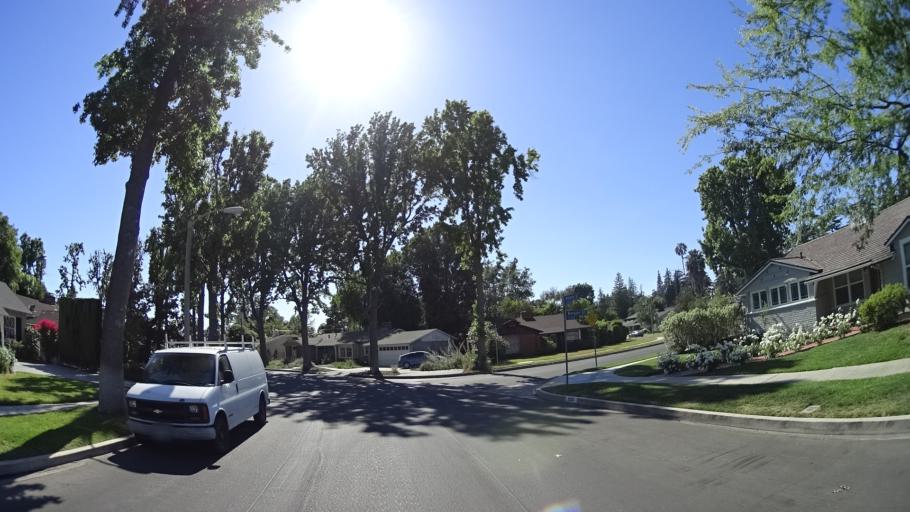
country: US
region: California
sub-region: Los Angeles County
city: Sherman Oaks
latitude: 34.1670
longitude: -118.4204
